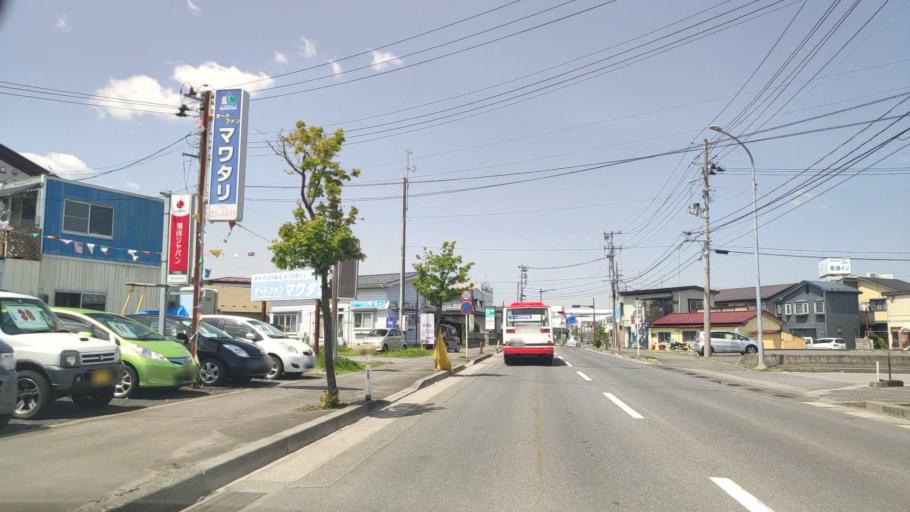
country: JP
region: Aomori
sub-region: Hachinohe Shi
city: Uchimaru
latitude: 40.5066
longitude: 141.4366
